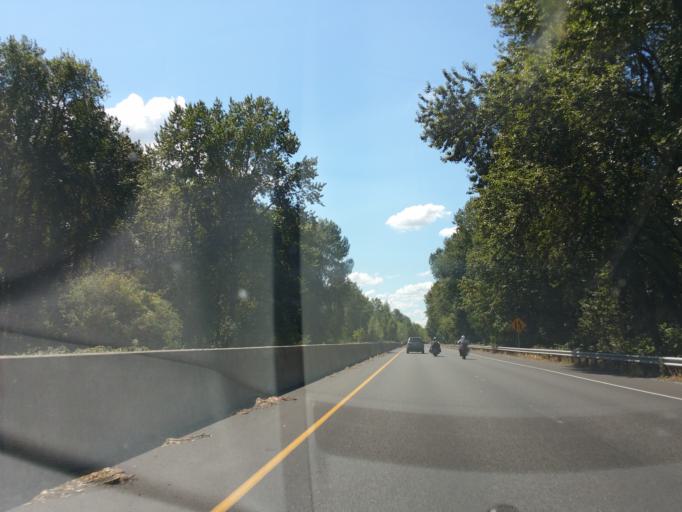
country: US
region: Washington
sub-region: Clark County
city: Camas
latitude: 45.5759
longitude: -122.4110
